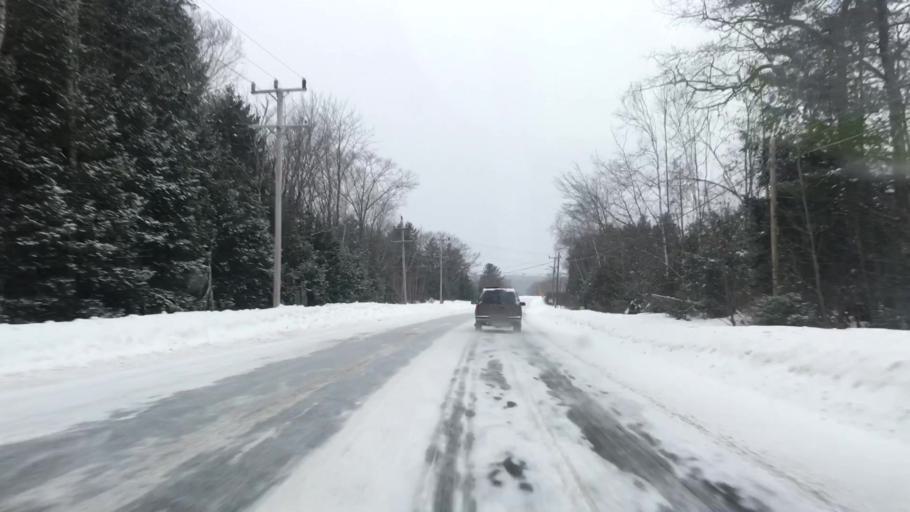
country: US
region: Maine
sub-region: Penobscot County
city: Medway
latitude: 45.5952
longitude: -68.4840
